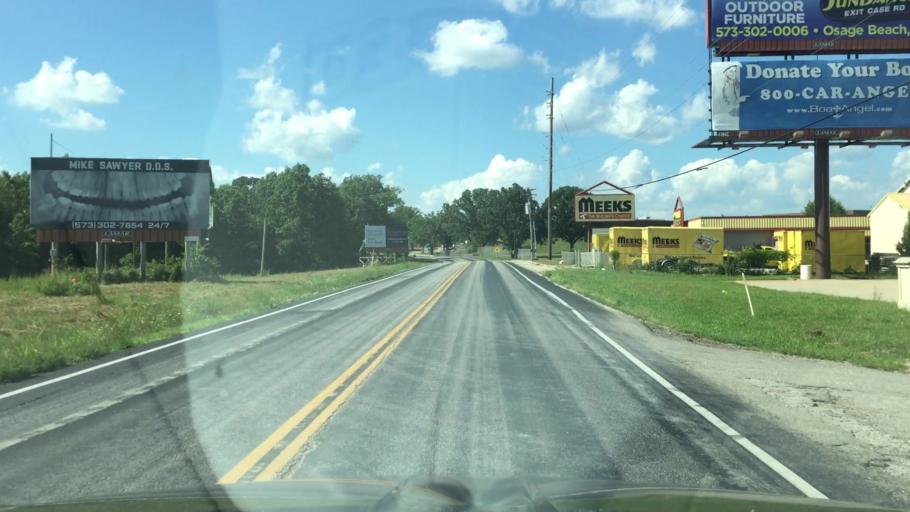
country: US
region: Missouri
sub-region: Camden County
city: Osage Beach
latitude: 38.1429
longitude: -92.5914
